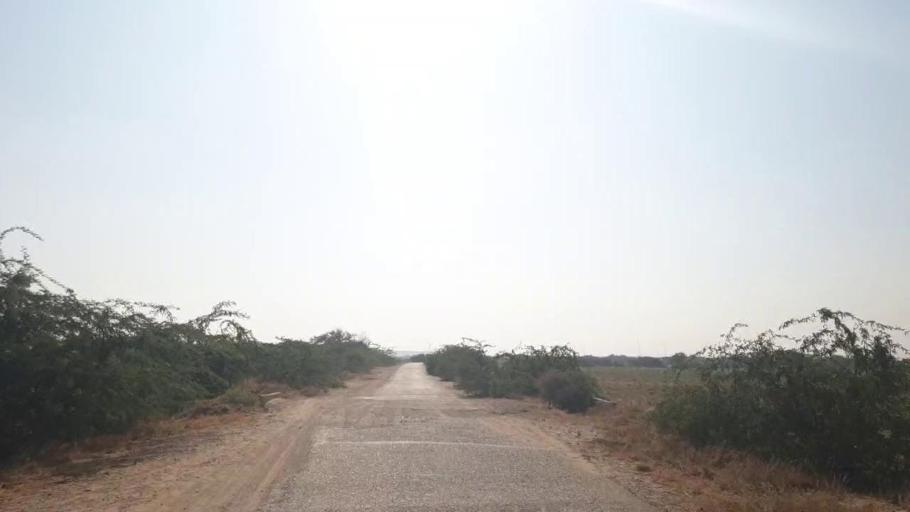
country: PK
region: Sindh
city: Thatta
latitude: 25.1319
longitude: 67.7748
